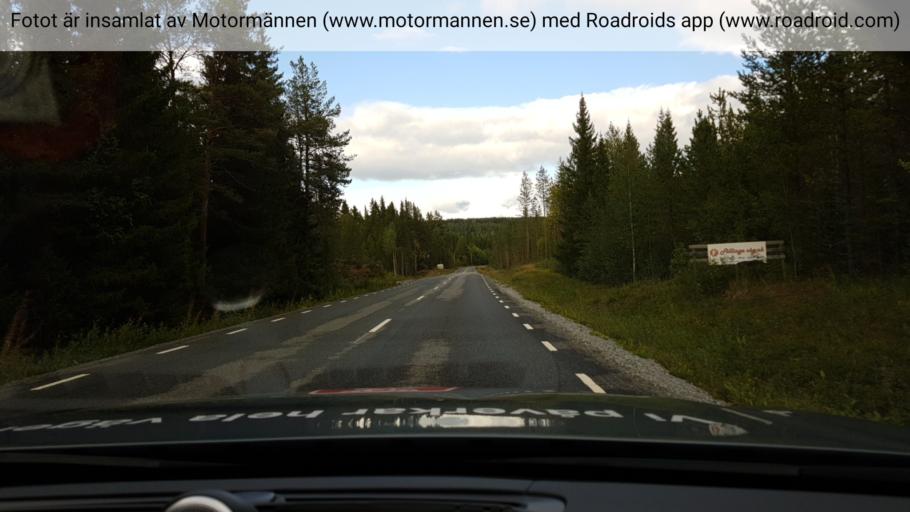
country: SE
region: Jaemtland
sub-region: Krokoms Kommun
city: Krokom
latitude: 63.6742
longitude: 14.5638
